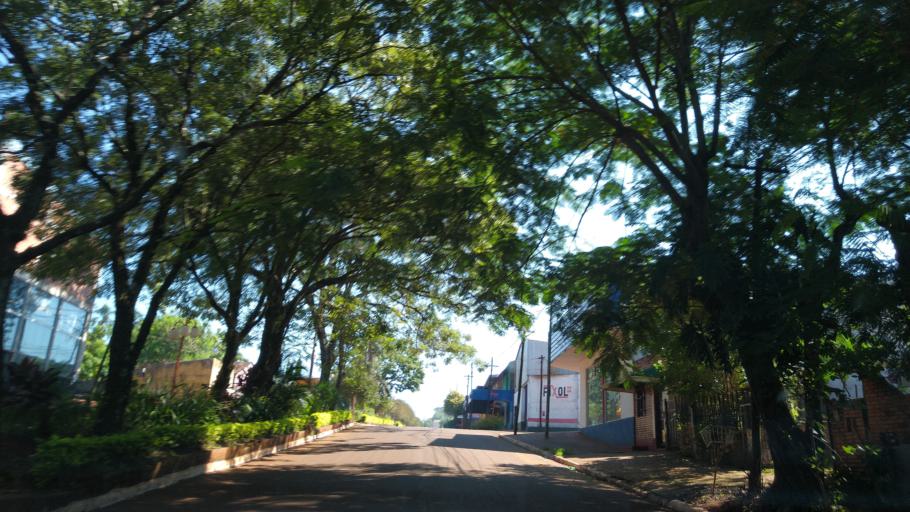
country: AR
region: Misiones
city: Puerto Esperanza
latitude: -26.0261
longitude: -54.6123
